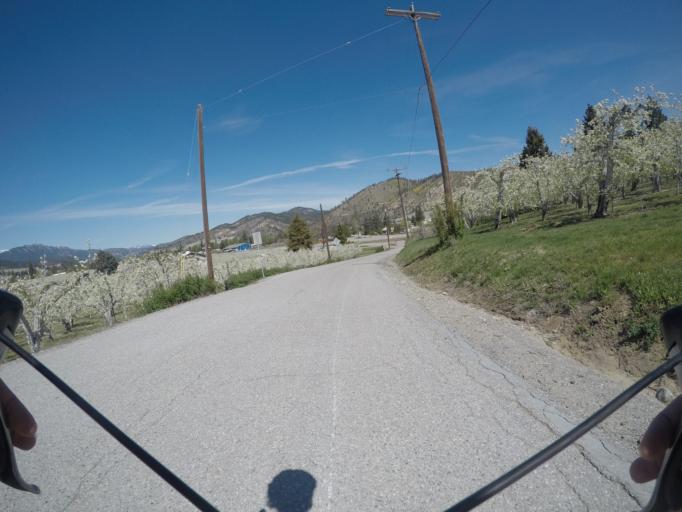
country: US
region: Washington
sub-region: Chelan County
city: Leavenworth
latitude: 47.5517
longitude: -120.5829
